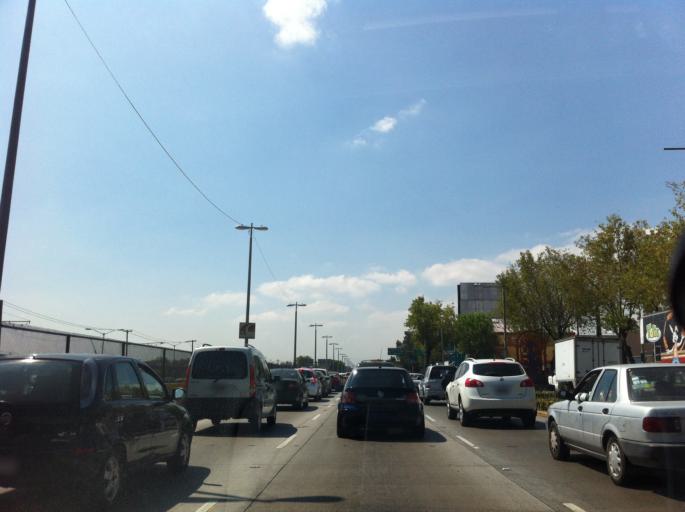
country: MX
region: Mexico City
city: Venustiano Carranza
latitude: 19.4300
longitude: -99.0908
